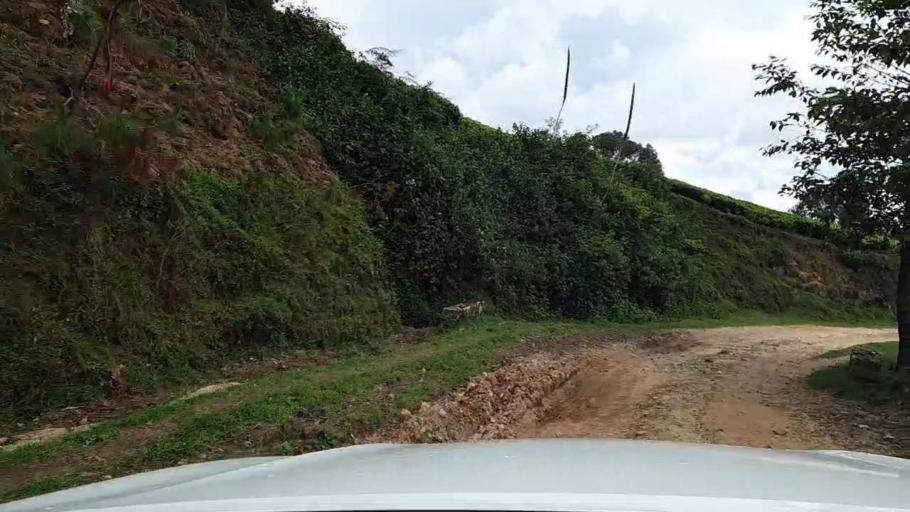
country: RW
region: Western Province
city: Kibuye
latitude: -2.2897
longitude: 29.3708
